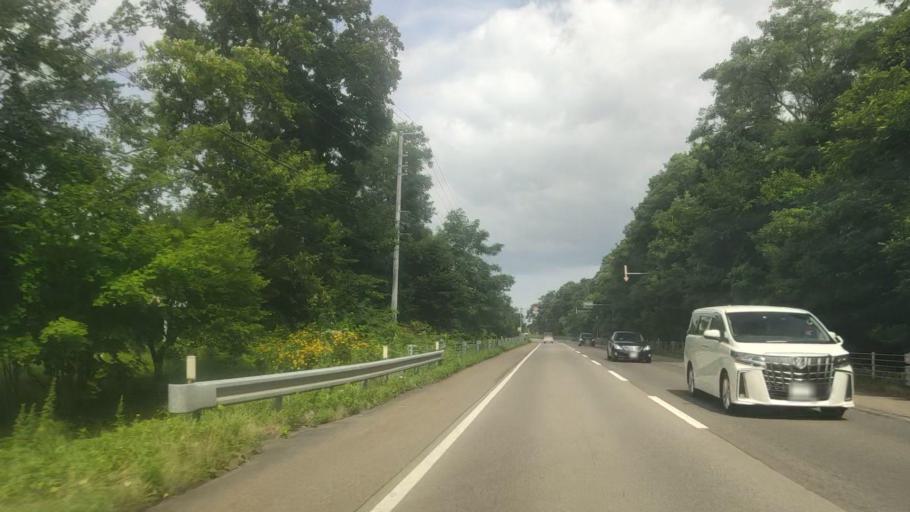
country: JP
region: Hokkaido
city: Nanae
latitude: 42.0524
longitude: 140.5992
